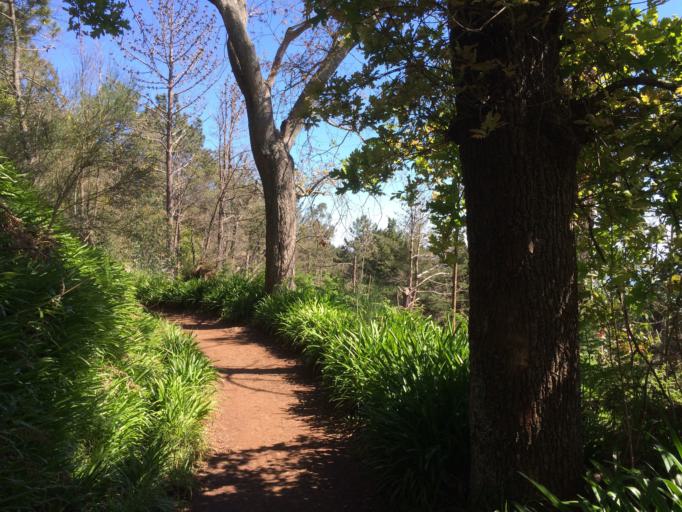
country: PT
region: Madeira
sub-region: Santa Cruz
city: Camacha
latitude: 32.6784
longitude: -16.8603
